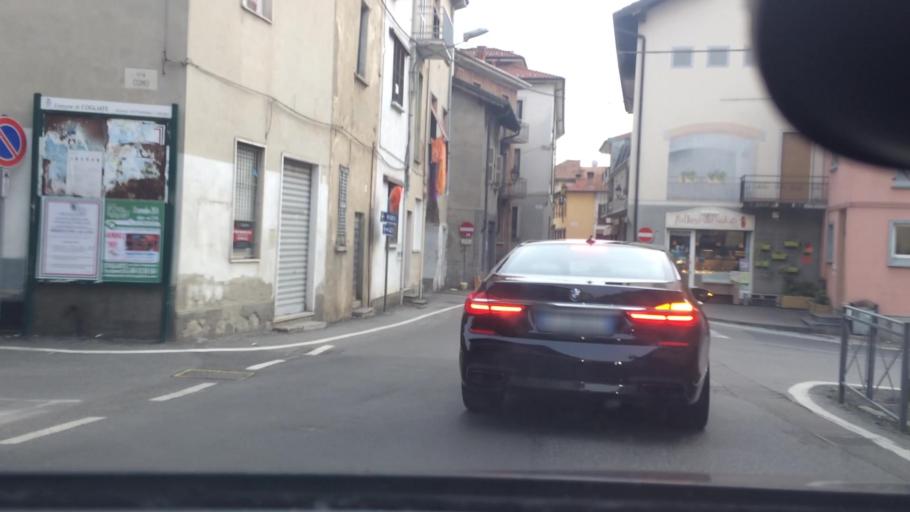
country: IT
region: Lombardy
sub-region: Provincia di Monza e Brianza
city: Cogliate
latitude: 45.6464
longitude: 9.0816
